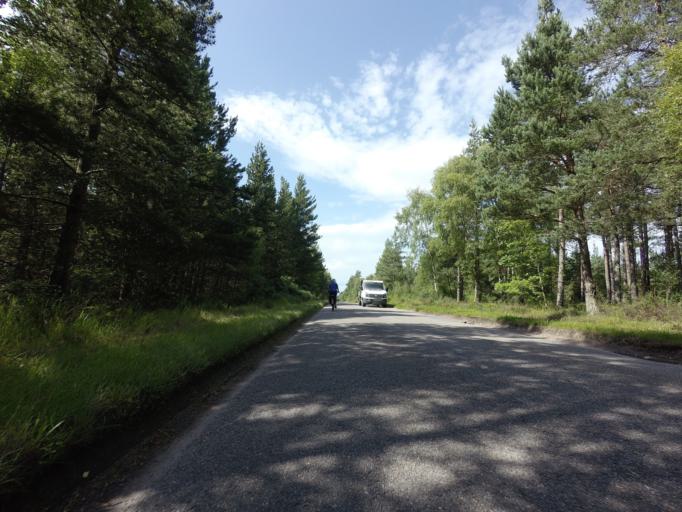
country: GB
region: Scotland
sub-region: Highland
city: Fortrose
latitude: 57.4809
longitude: -4.0890
